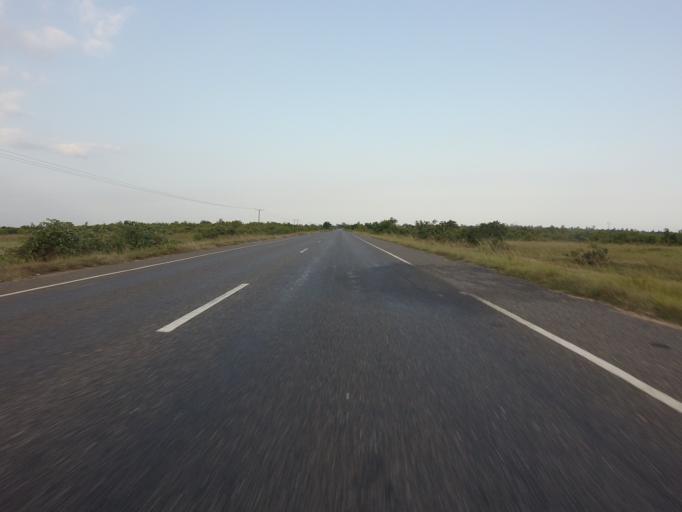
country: GH
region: Volta
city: Anloga
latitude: 6.0772
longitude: 0.5954
